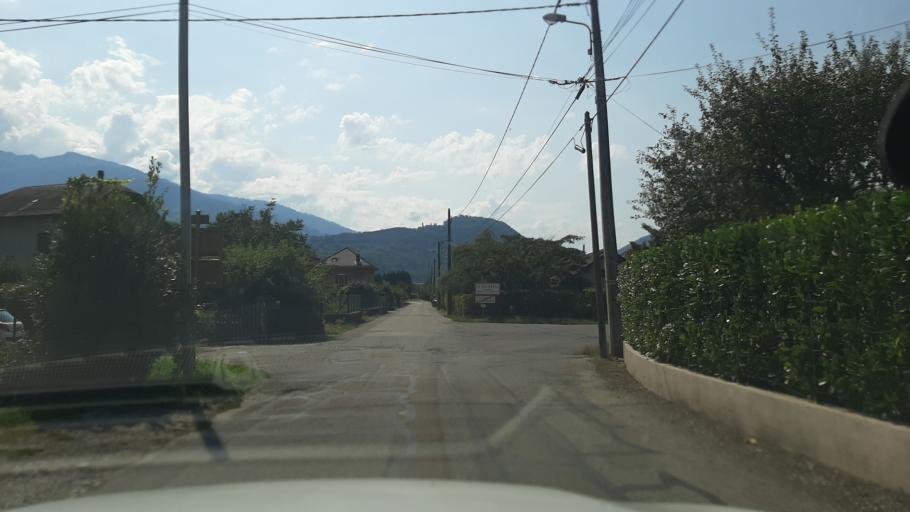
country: FR
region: Rhone-Alpes
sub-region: Departement de la Savoie
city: La Rochette
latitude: 45.4661
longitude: 6.1179
